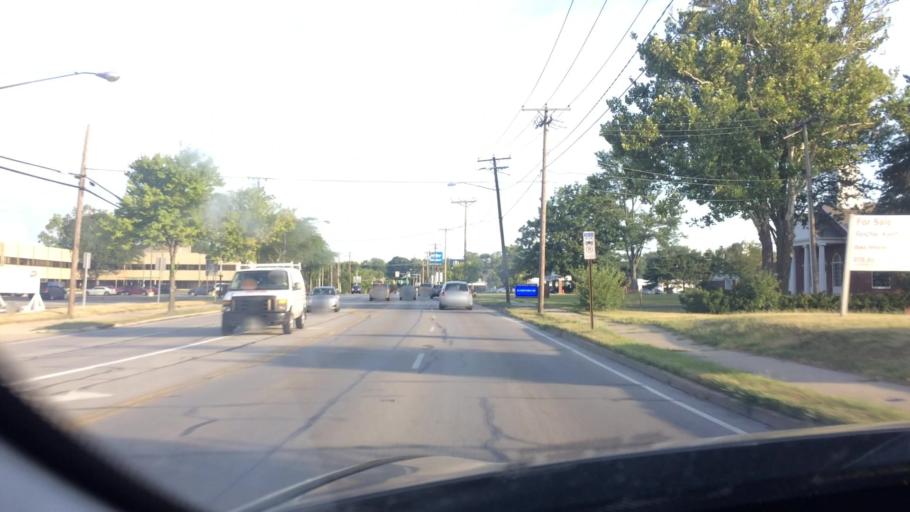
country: US
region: Ohio
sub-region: Lucas County
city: Sylvania
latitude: 41.7124
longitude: -83.6817
